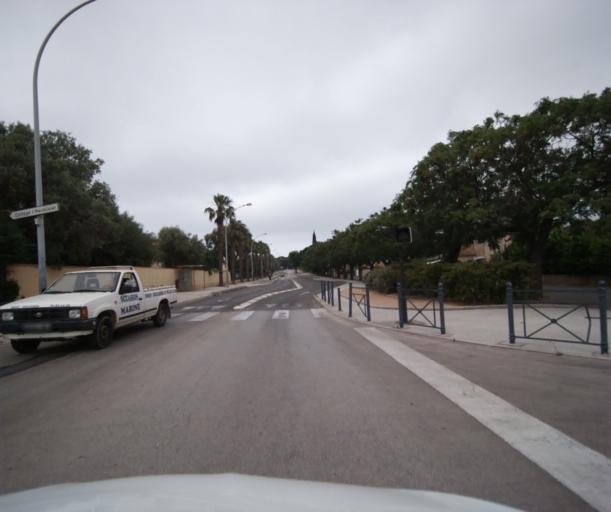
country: FR
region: Provence-Alpes-Cote d'Azur
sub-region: Departement du Var
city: La Seyne-sur-Mer
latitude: 43.0877
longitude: 5.8908
